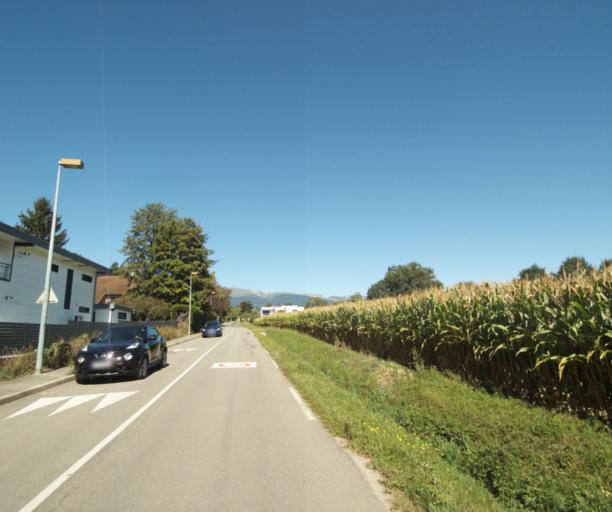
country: FR
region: Rhone-Alpes
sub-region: Departement de l'Ain
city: Ornex
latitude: 46.2614
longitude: 6.0971
